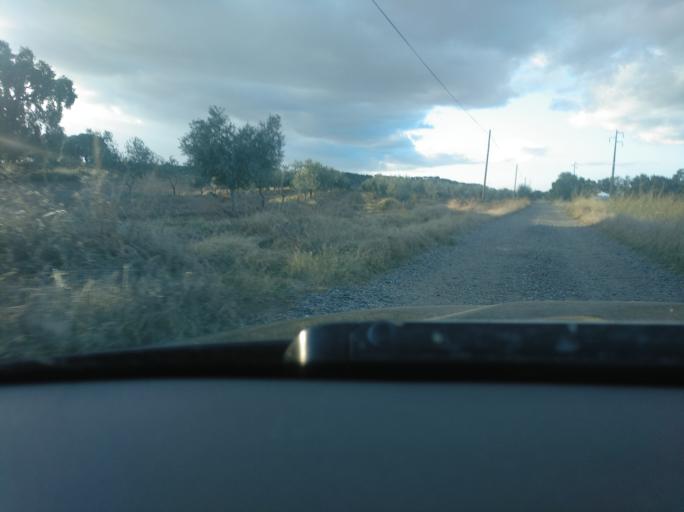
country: PT
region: Portalegre
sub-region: Campo Maior
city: Campo Maior
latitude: 39.0386
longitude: -6.9896
